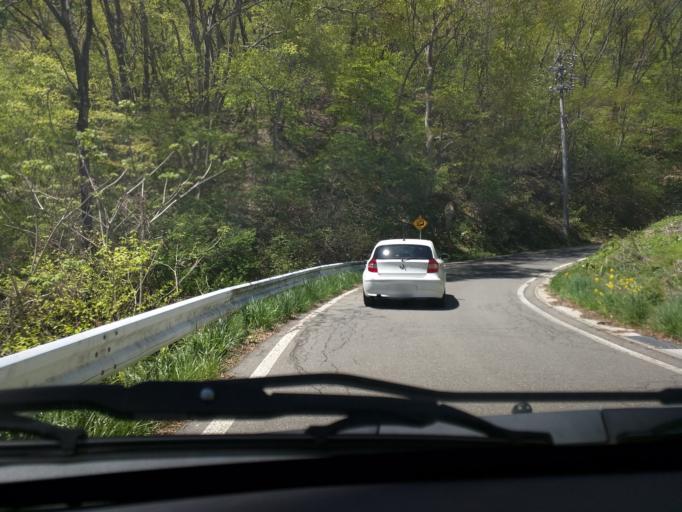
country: JP
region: Nagano
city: Nagano-shi
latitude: 36.6888
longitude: 138.1092
